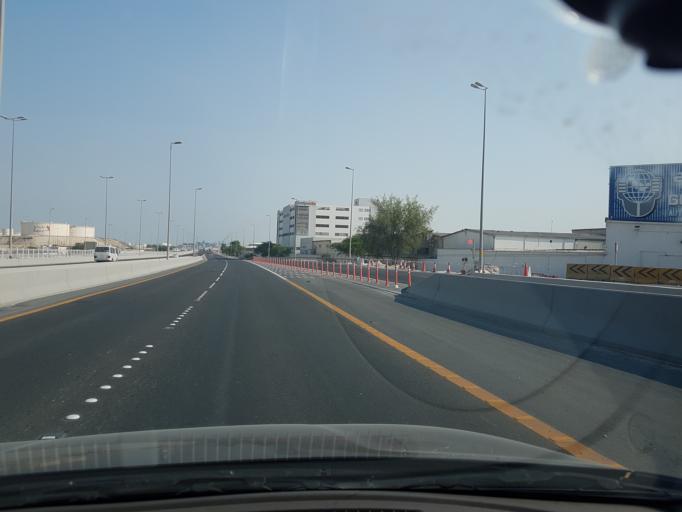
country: BH
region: Northern
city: Ar Rifa'
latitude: 26.1195
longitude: 50.5927
